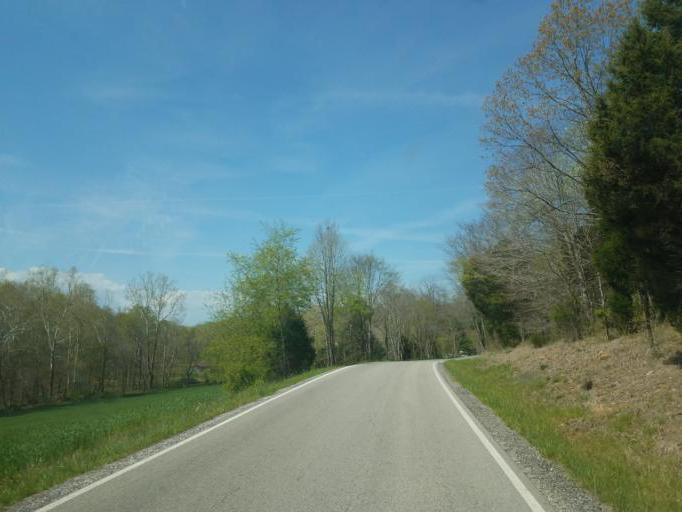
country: US
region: Kentucky
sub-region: Edmonson County
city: Brownsville
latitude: 37.2840
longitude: -86.3930
